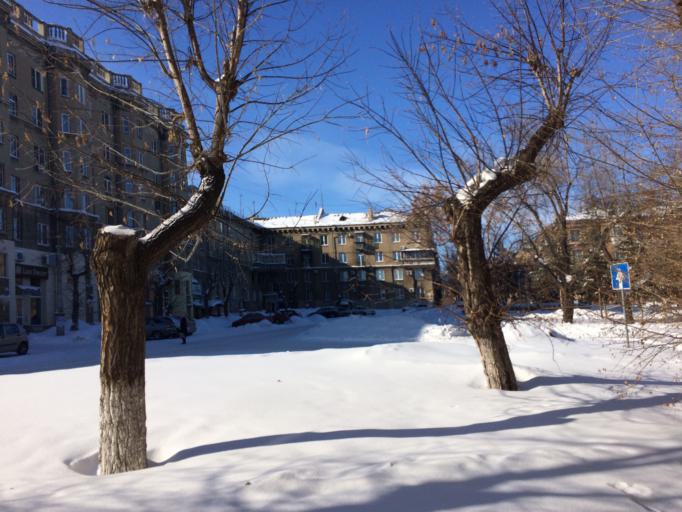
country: RU
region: Chelyabinsk
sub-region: Gorod Magnitogorsk
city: Magnitogorsk
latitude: 53.4201
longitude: 58.9969
